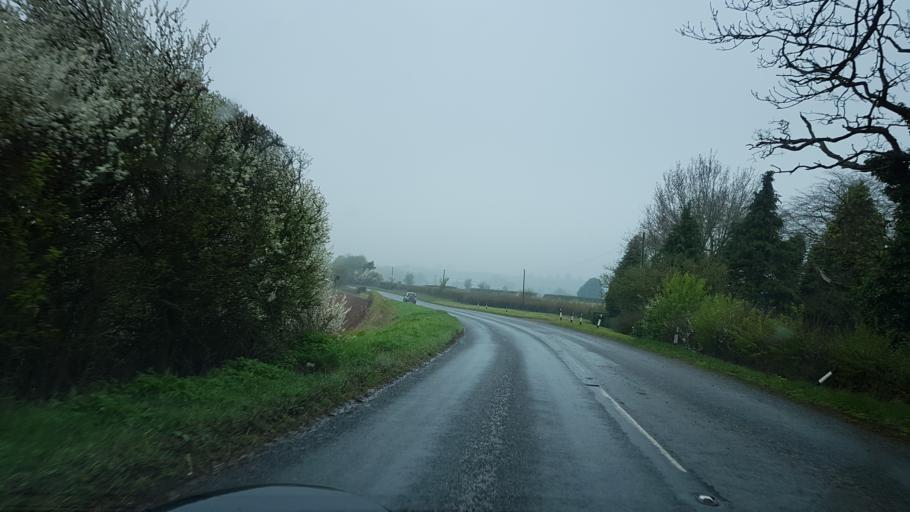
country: GB
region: England
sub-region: Herefordshire
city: Bromyard
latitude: 52.1723
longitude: -2.5287
